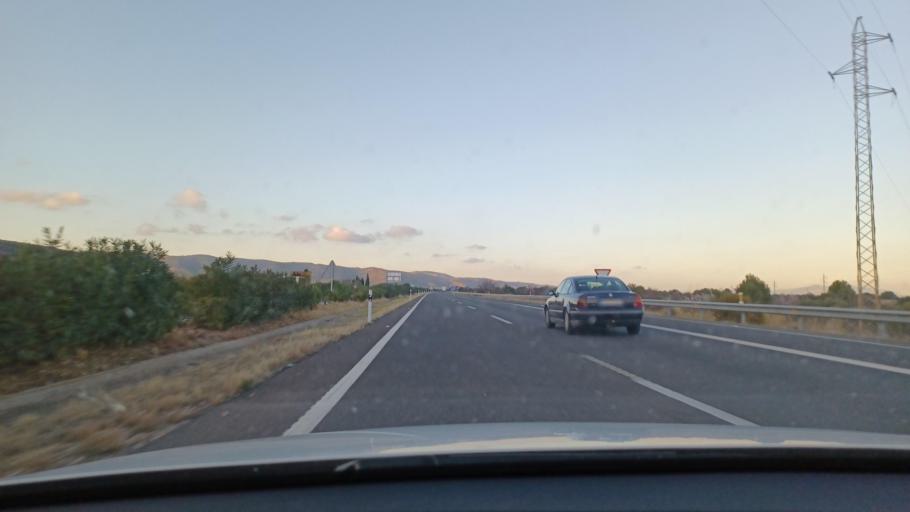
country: ES
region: Valencia
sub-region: Provincia de Castello
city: Orpesa/Oropesa del Mar
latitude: 40.1097
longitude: 0.1313
